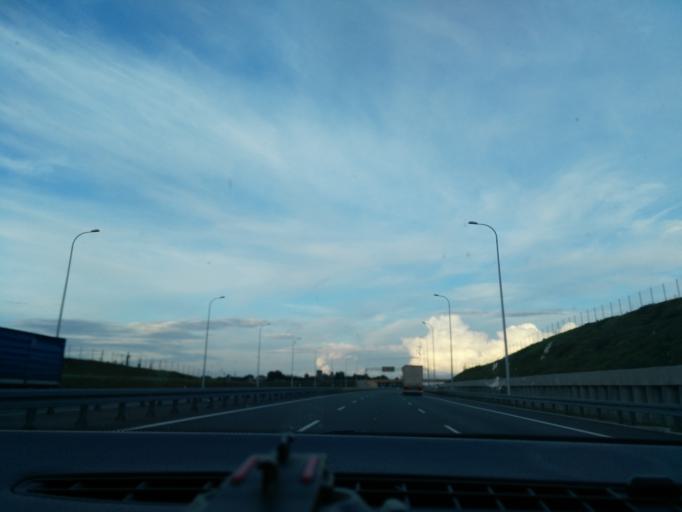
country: PL
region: Lublin Voivodeship
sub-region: Powiat lubelski
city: Jastkow
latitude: 51.3013
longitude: 22.5095
